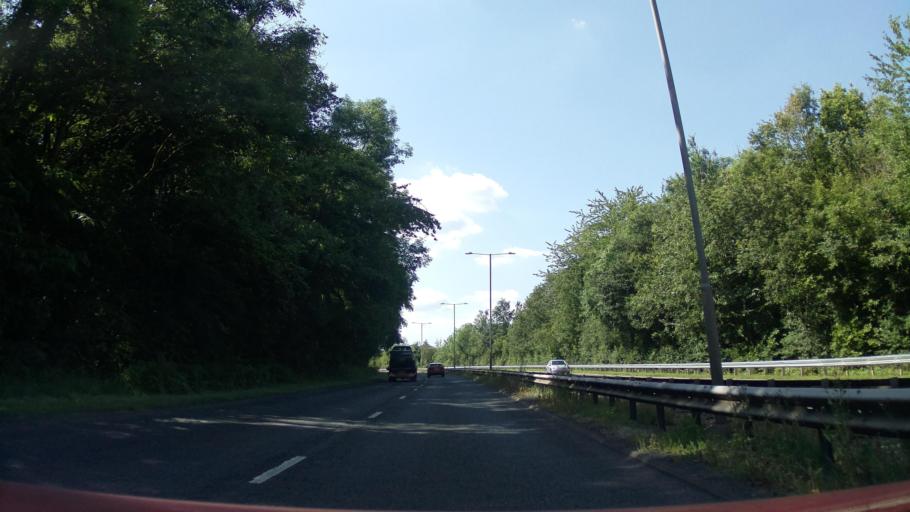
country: GB
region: England
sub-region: Worcestershire
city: Redditch
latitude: 52.3010
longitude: -1.9655
